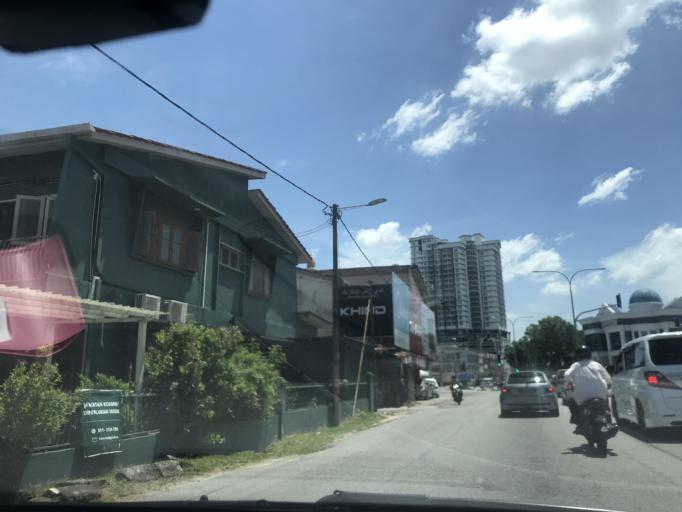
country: MY
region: Kelantan
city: Kota Bharu
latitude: 6.1267
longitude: 102.2472
